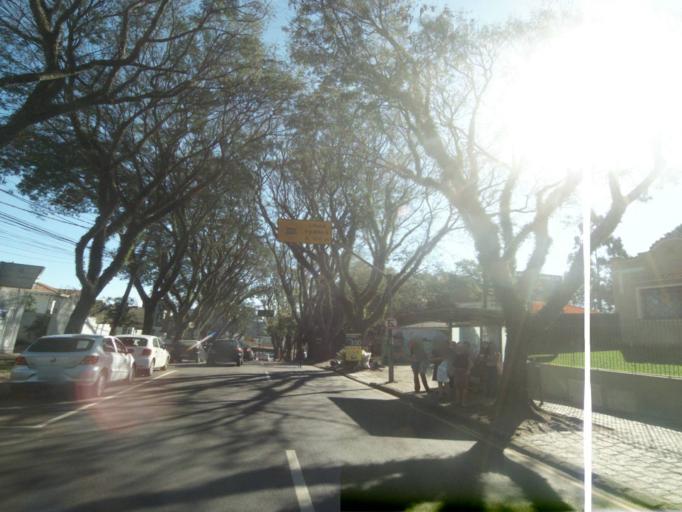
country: BR
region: Parana
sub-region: Curitiba
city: Curitiba
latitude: -25.4034
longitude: -49.2451
